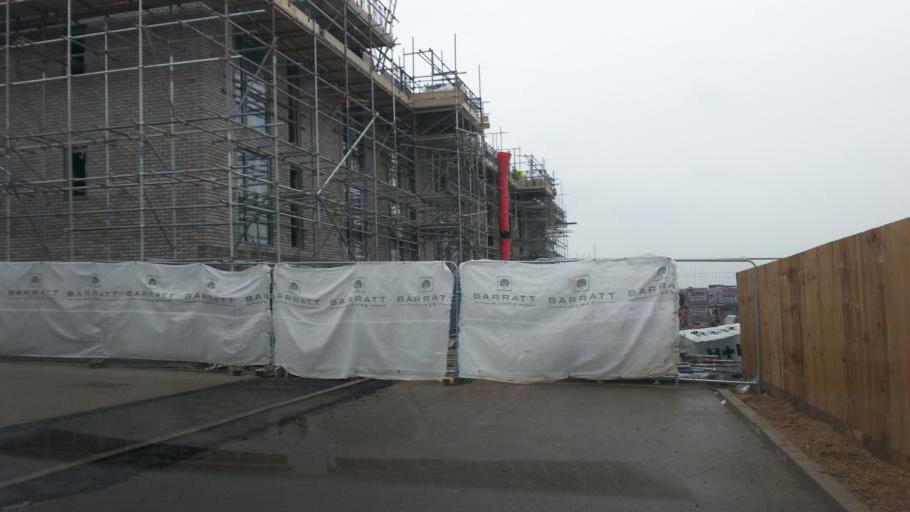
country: GB
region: England
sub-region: Cambridgeshire
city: Grantchester
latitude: 52.1699
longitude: 0.1031
